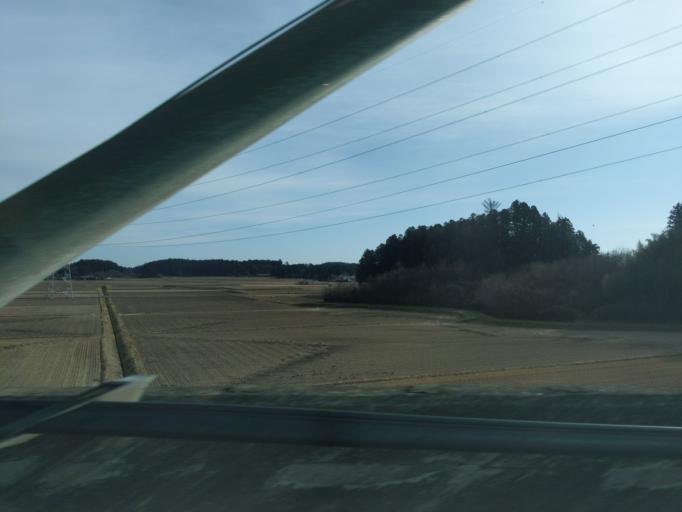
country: JP
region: Miyagi
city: Furukawa
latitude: 38.6190
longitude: 140.9960
